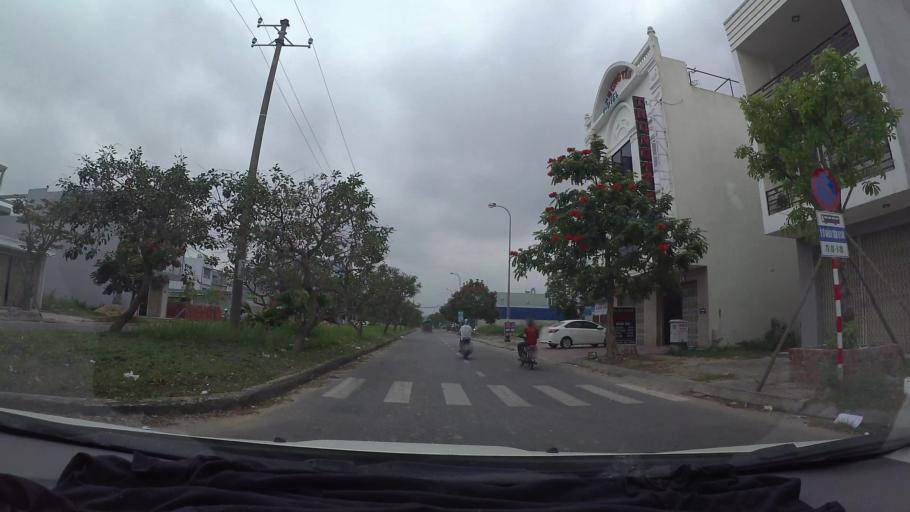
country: VN
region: Da Nang
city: Lien Chieu
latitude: 16.0620
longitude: 108.1712
